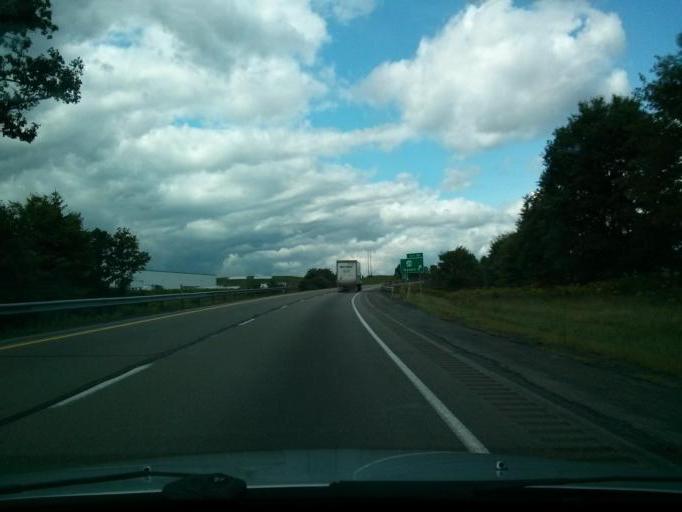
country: US
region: Pennsylvania
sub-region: Jefferson County
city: Brookville
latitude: 41.1686
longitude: -79.0381
